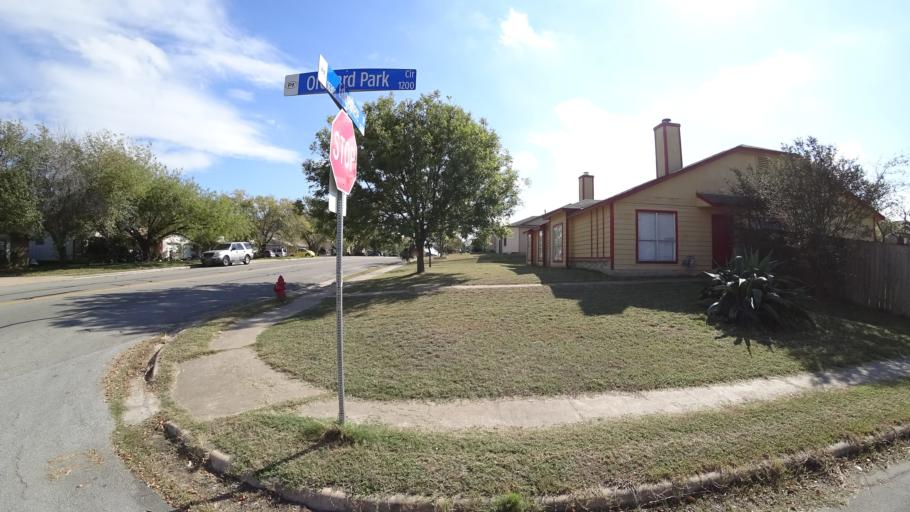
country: US
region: Texas
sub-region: Travis County
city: Windemere
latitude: 30.4556
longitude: -97.6511
